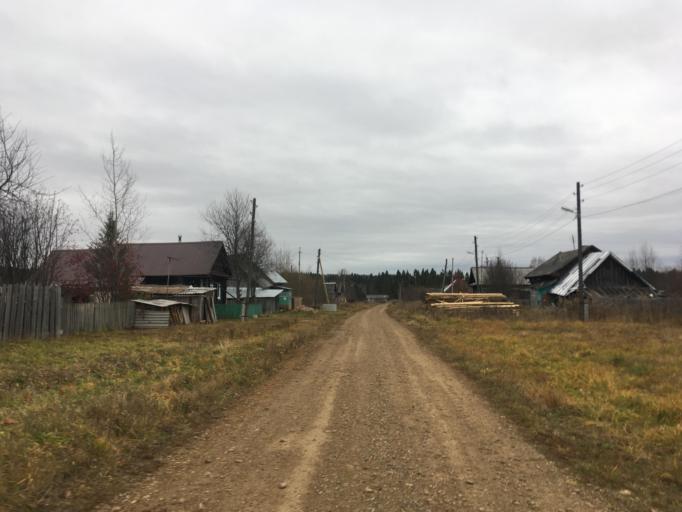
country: RU
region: Perm
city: Komarikhinskiy
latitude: 58.0907
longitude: 57.1109
